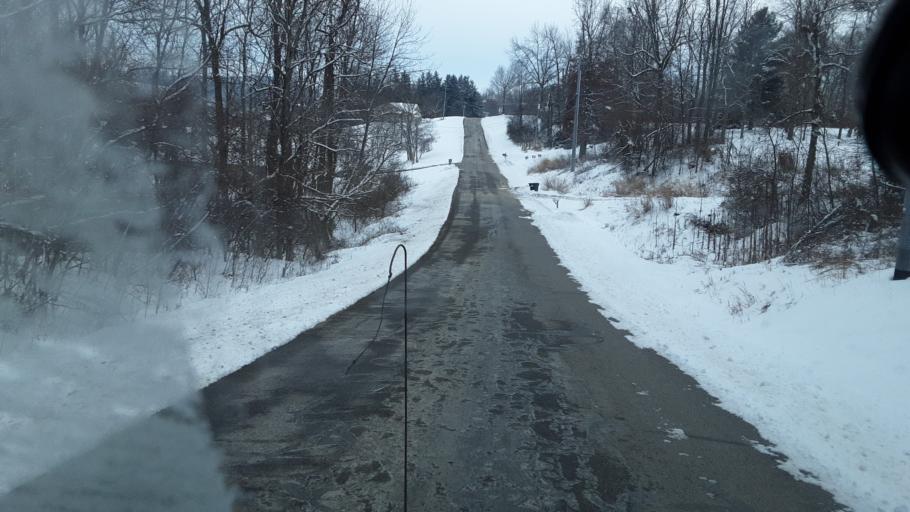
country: US
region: Ohio
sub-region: Perry County
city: Thornport
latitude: 39.9591
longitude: -82.3416
